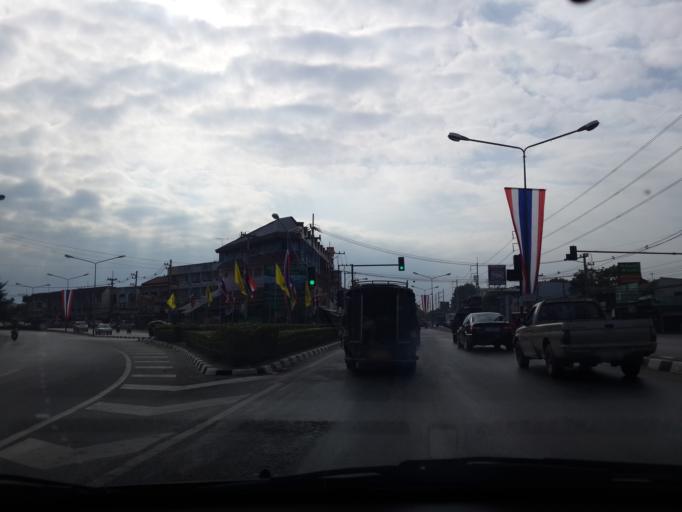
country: TH
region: Chiang Mai
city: San Sai
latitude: 18.8933
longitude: 99.0103
